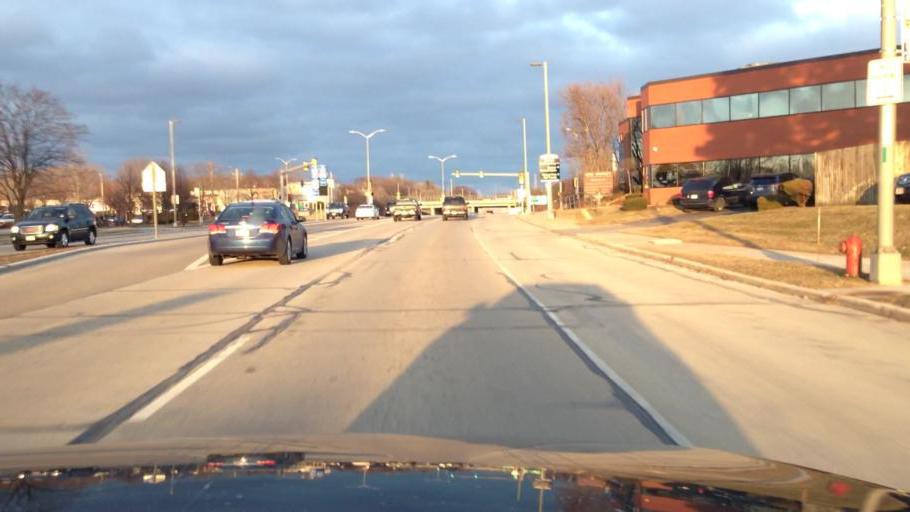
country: US
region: Wisconsin
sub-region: Milwaukee County
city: Greenfield
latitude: 42.9570
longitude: -88.0195
